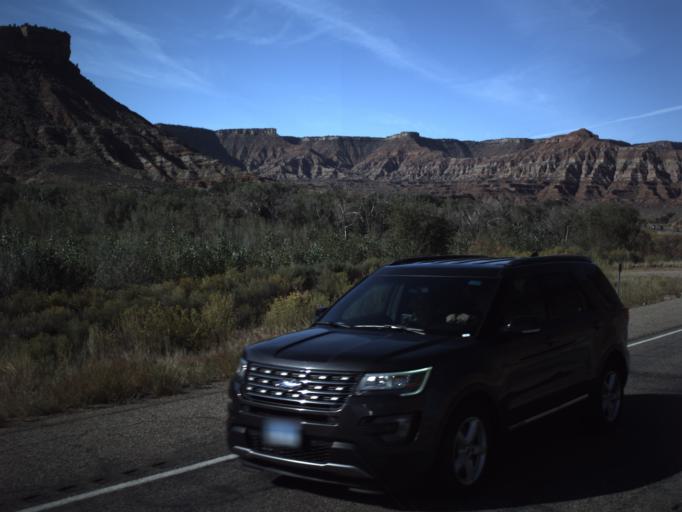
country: US
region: Utah
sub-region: Washington County
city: LaVerkin
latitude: 37.1718
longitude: -113.0908
